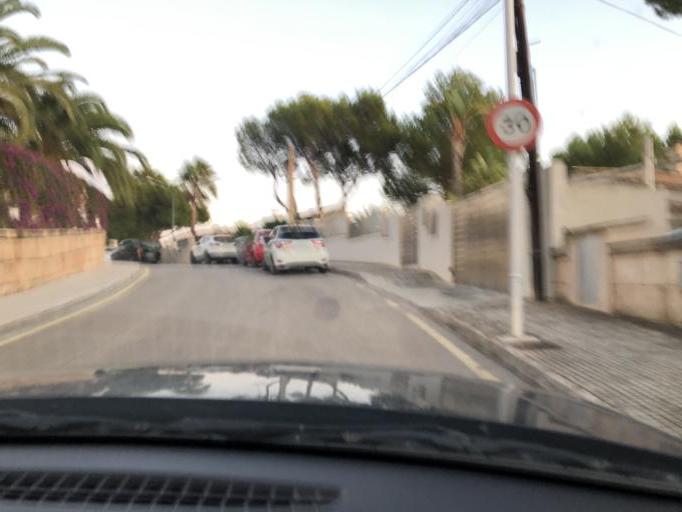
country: ES
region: Balearic Islands
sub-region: Illes Balears
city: Santa Ponsa
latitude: 39.5277
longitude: 2.4718
